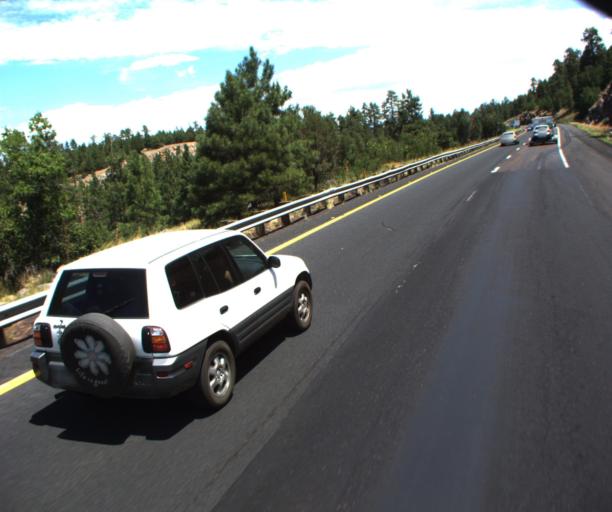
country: US
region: Arizona
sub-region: Yavapai County
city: Village of Oak Creek (Big Park)
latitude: 34.8231
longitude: -111.6110
